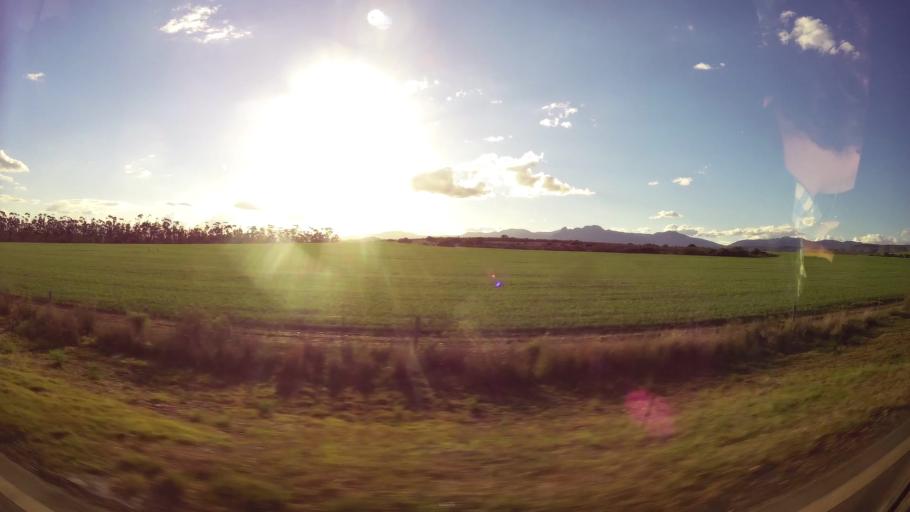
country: ZA
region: Western Cape
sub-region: Eden District Municipality
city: Riversdale
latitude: -34.0884
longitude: 20.9800
